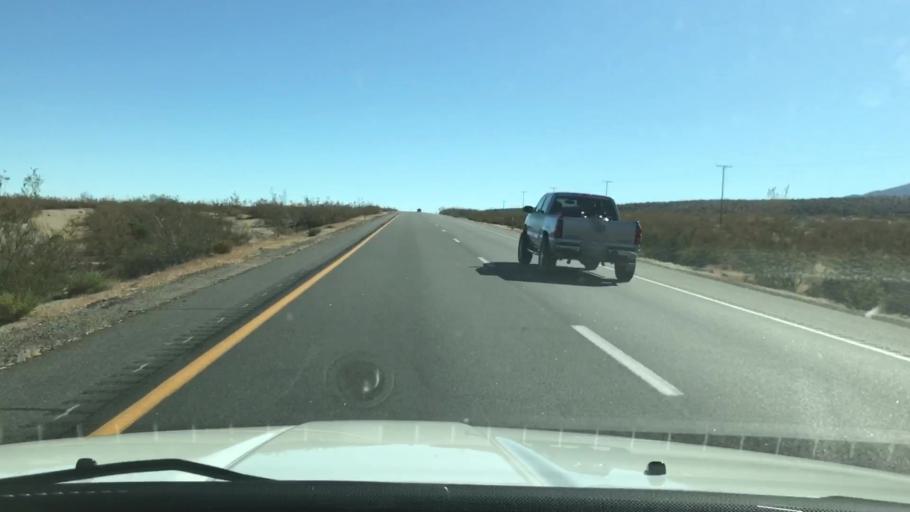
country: US
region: California
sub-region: Kern County
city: Inyokern
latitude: 35.8794
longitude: -117.8903
